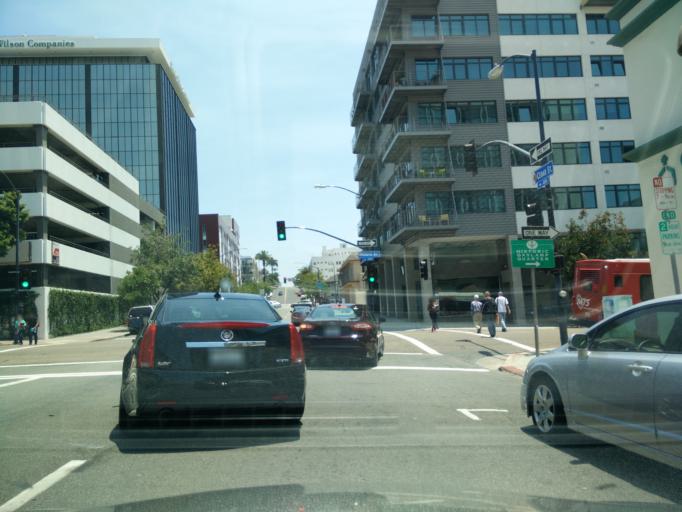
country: US
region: California
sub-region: San Diego County
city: San Diego
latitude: 32.7219
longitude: -117.1614
